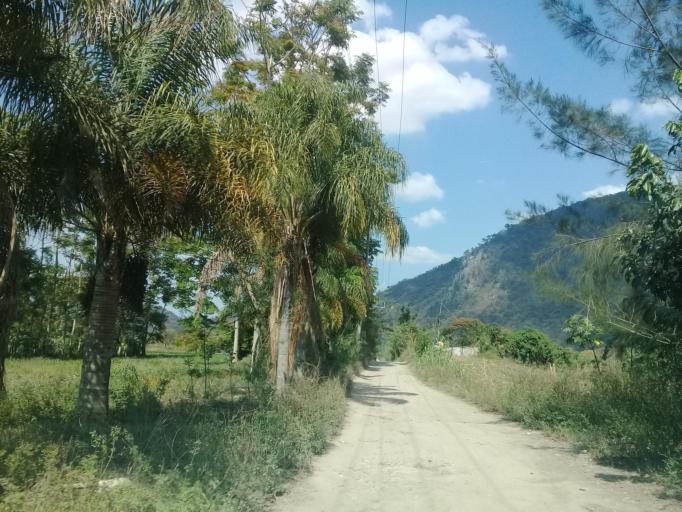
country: MX
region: Veracruz
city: Jalapilla
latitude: 18.8265
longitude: -97.0761
